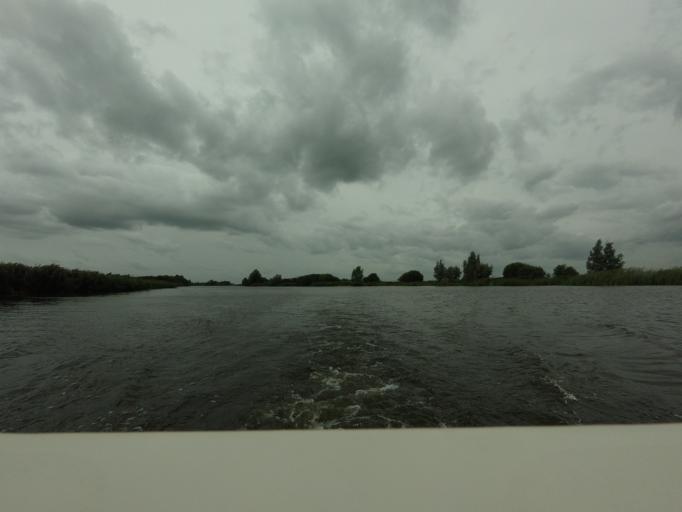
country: NL
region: Friesland
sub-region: Gemeente Boarnsterhim
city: Warten
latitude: 53.1002
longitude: 5.9158
